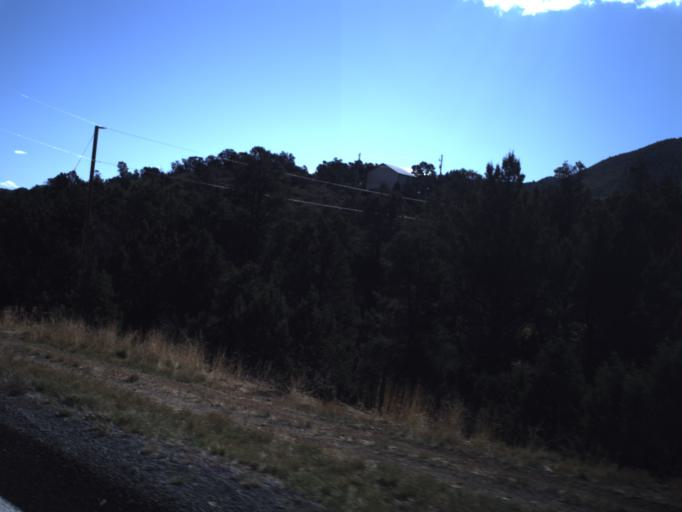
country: US
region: Utah
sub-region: Iron County
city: Cedar City
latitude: 37.6078
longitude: -113.3574
